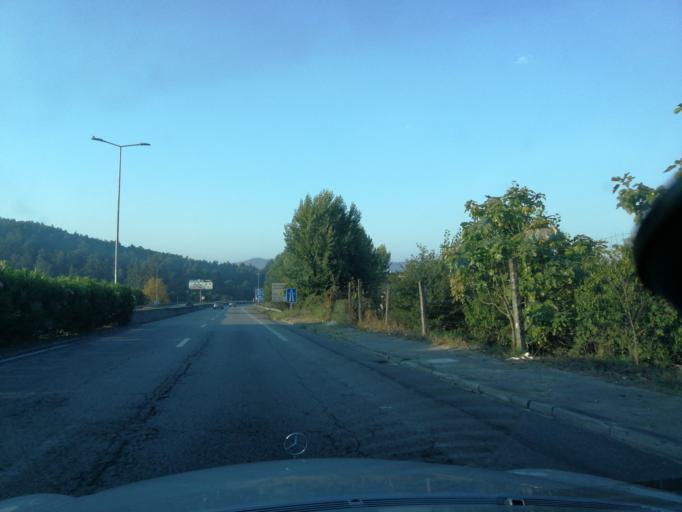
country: PT
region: Braga
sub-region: Braga
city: Braga
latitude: 41.5277
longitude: -8.4143
